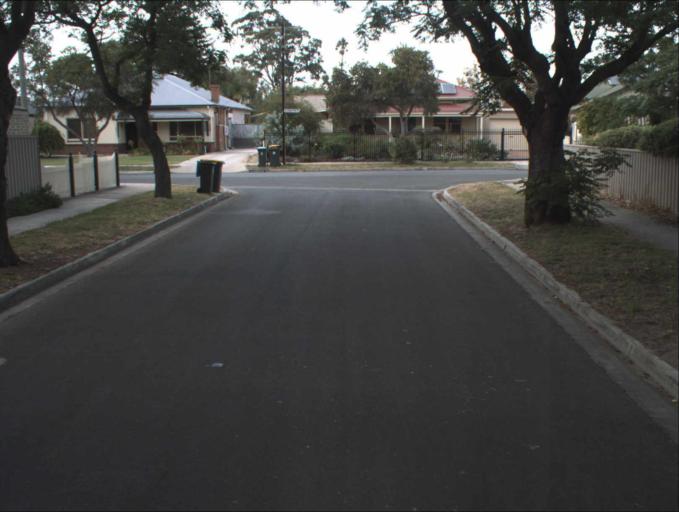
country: AU
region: South Australia
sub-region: Port Adelaide Enfield
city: Birkenhead
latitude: -34.8272
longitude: 138.4945
